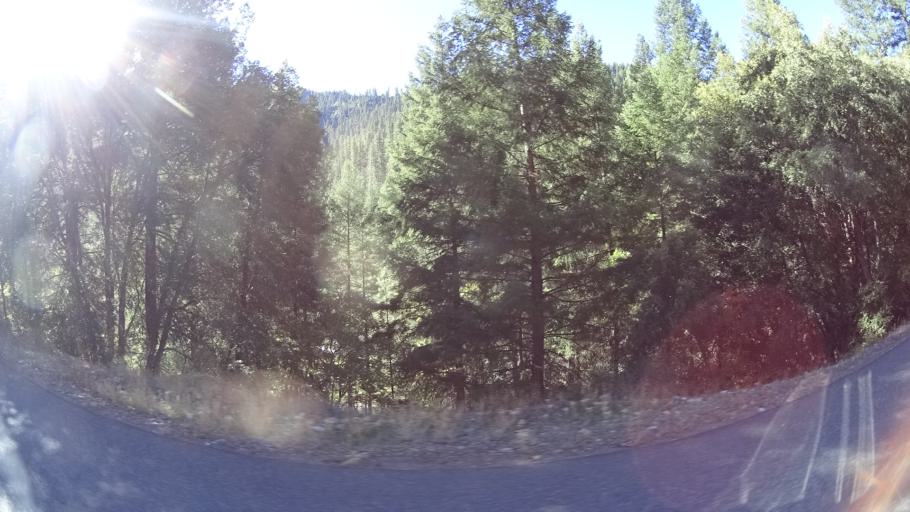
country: US
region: California
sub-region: Trinity County
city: Weaverville
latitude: 41.1438
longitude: -123.1872
